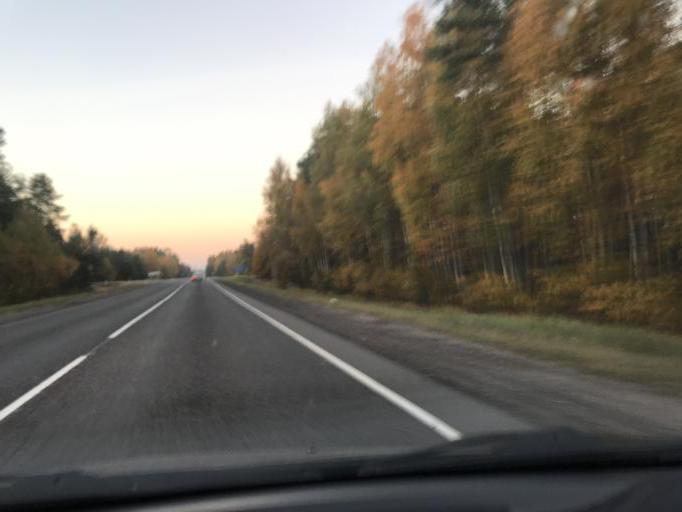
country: BY
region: Mogilev
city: Babruysk
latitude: 53.1631
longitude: 29.0457
